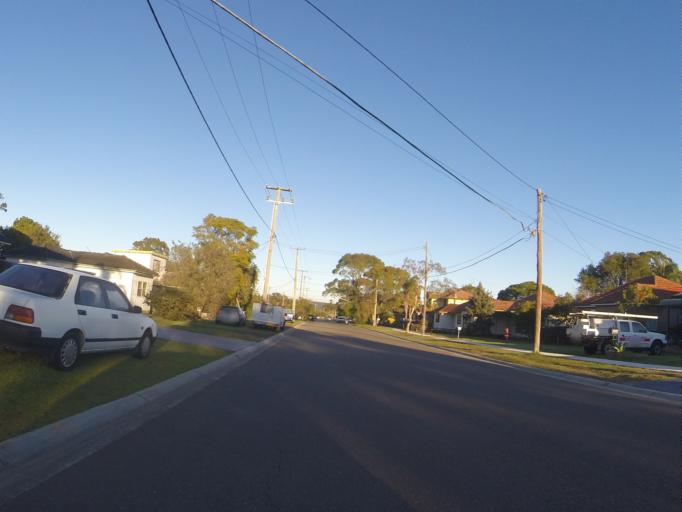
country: AU
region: New South Wales
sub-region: Sutherland Shire
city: Engadine
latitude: -34.0693
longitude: 151.0054
